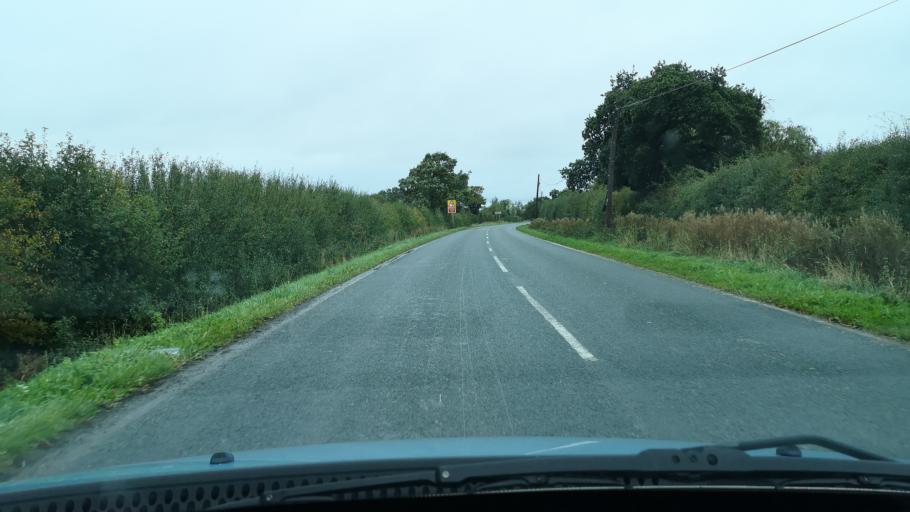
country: GB
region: England
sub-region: Doncaster
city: Moss
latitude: 53.6185
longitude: -1.0686
